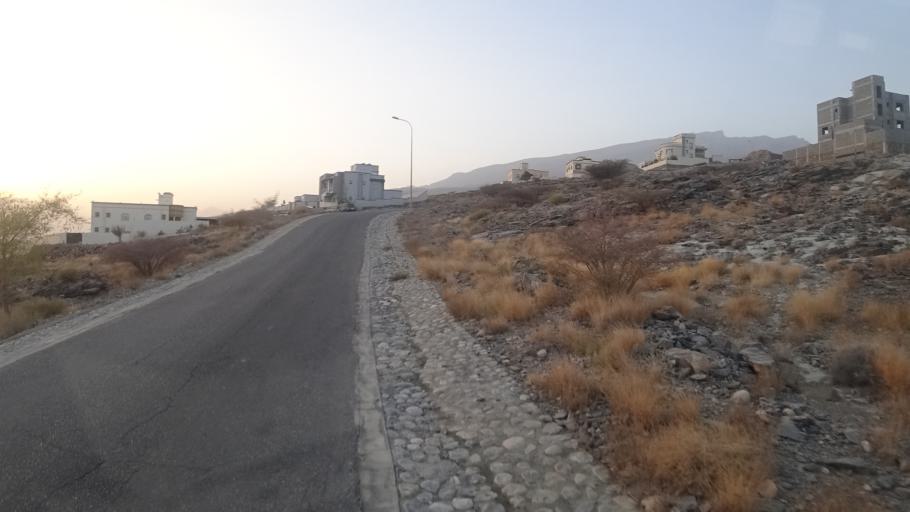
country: OM
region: Muhafazat ad Dakhiliyah
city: Bahla'
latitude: 23.1326
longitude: 57.3053
